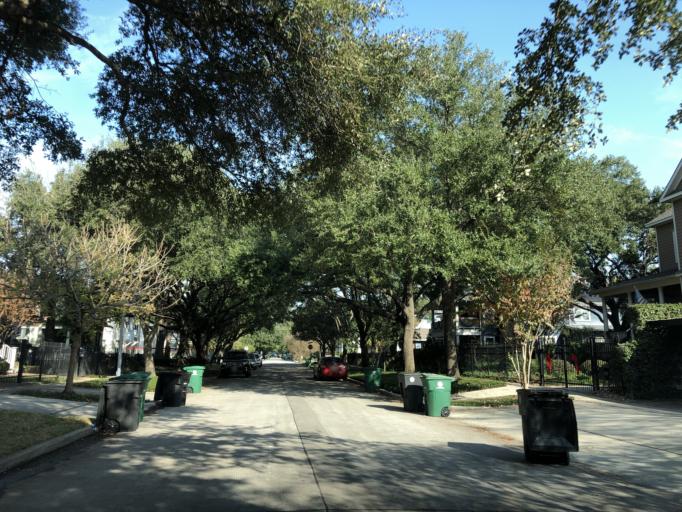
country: US
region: Texas
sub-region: Harris County
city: Houston
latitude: 29.7953
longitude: -95.3954
